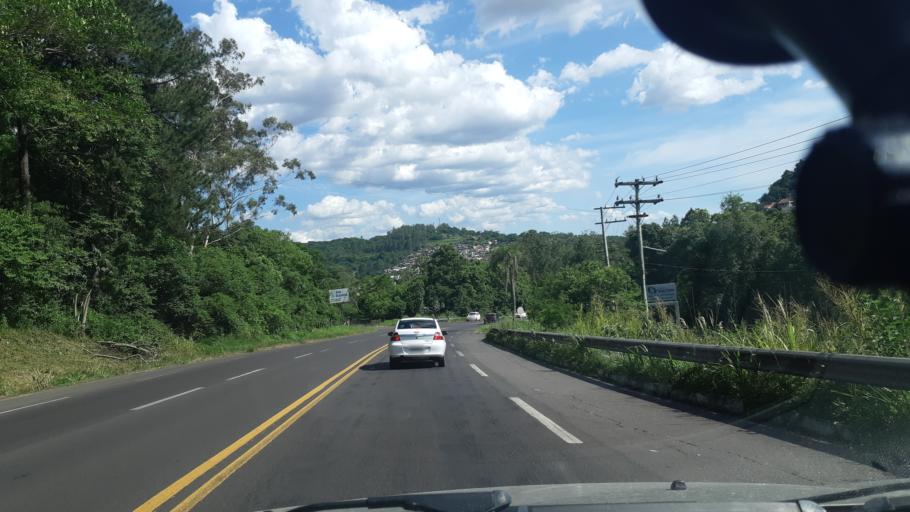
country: BR
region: Rio Grande do Sul
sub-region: Estancia Velha
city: Estancia Velha
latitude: -29.6367
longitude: -51.1421
